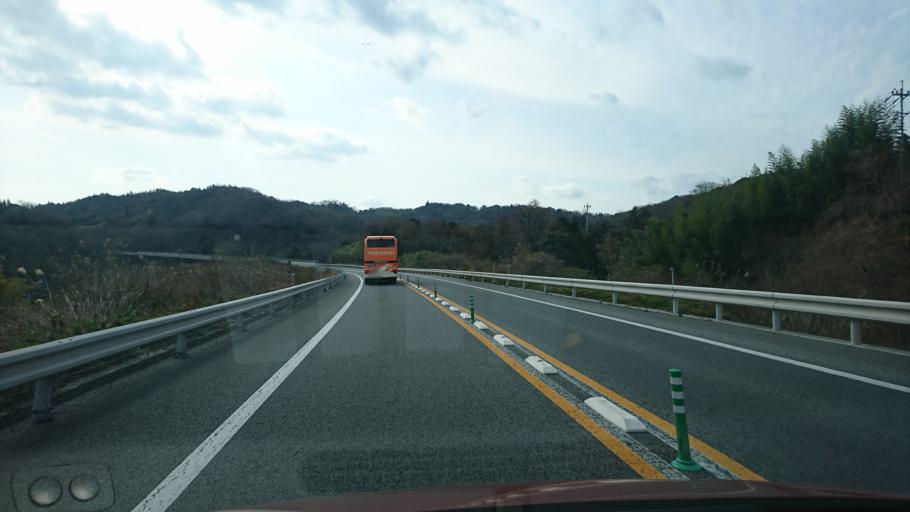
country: JP
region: Hiroshima
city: Innoshima
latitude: 34.1699
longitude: 133.0649
